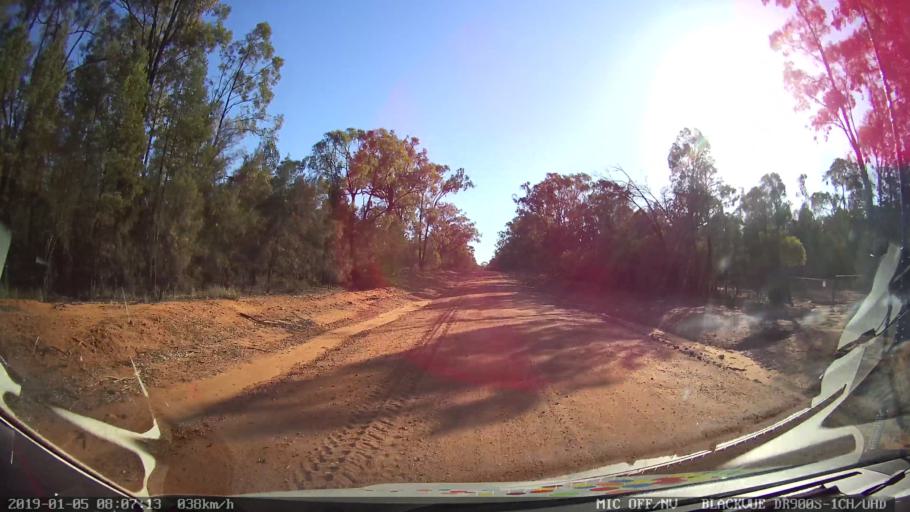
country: AU
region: New South Wales
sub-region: Gilgandra
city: Gilgandra
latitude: -31.6693
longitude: 148.7542
